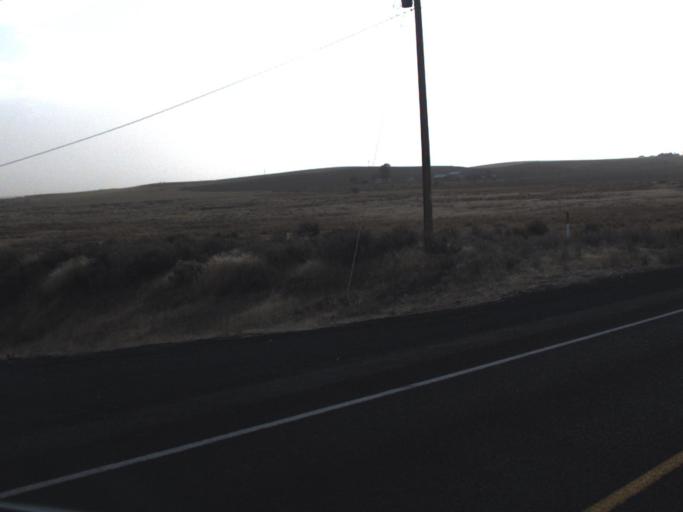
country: US
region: Washington
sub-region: Lincoln County
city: Davenport
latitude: 47.4751
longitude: -118.2767
